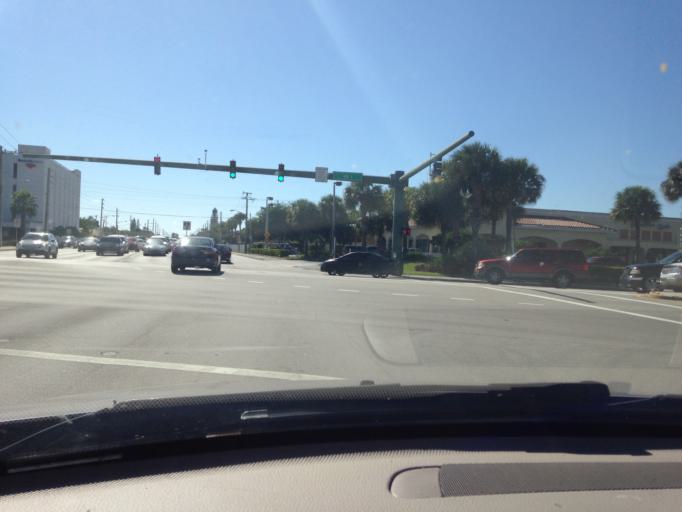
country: US
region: Florida
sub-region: Martin County
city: Stuart
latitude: 27.1914
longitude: -80.2531
